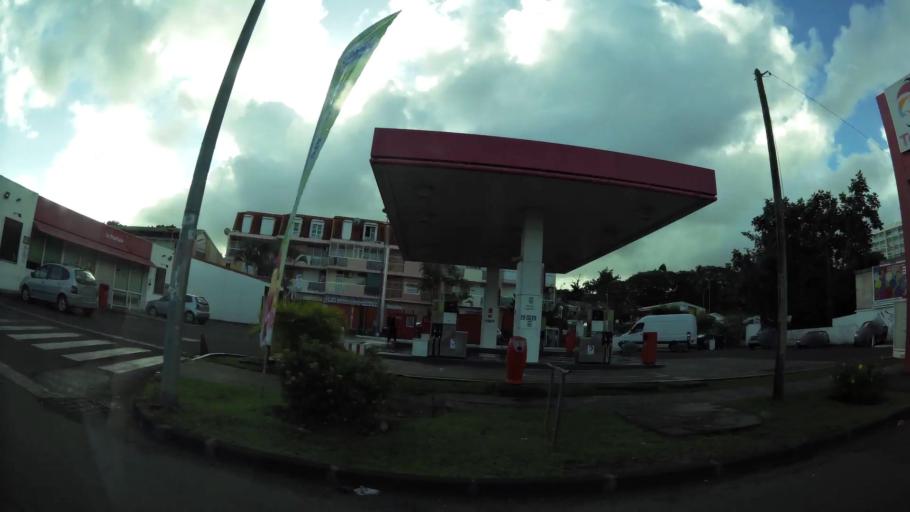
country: GP
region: Guadeloupe
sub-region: Guadeloupe
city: Pointe-a-Pitre
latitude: 16.2486
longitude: -61.5315
